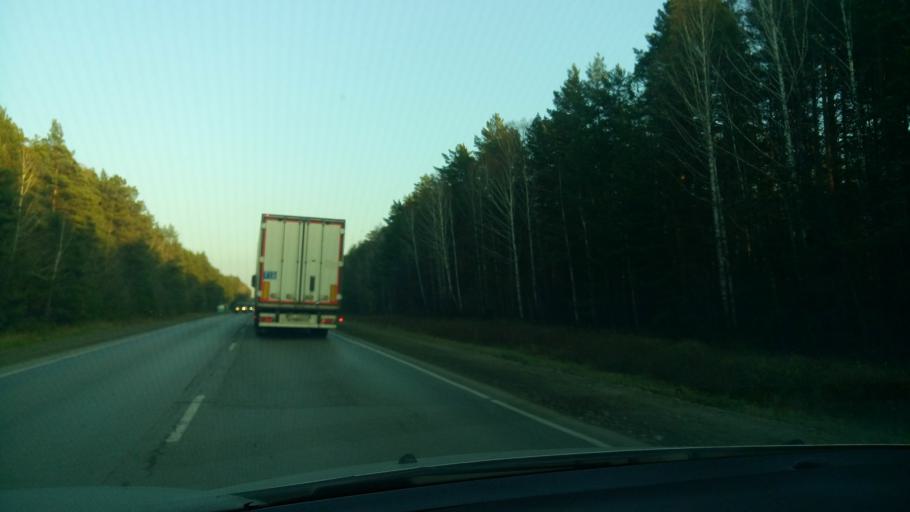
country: RU
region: Sverdlovsk
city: Yelanskiy
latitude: 56.7579
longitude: 62.3114
